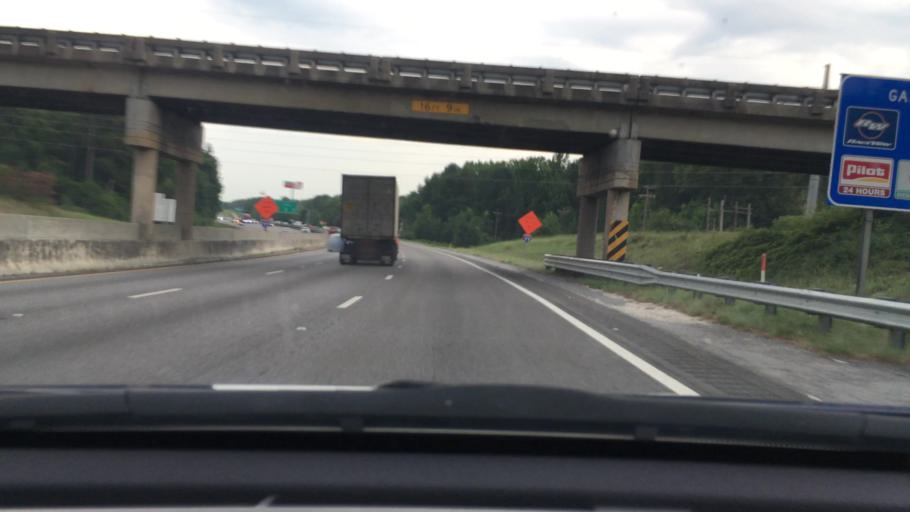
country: US
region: South Carolina
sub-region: Lexington County
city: Cayce
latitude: 33.9388
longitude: -81.0867
